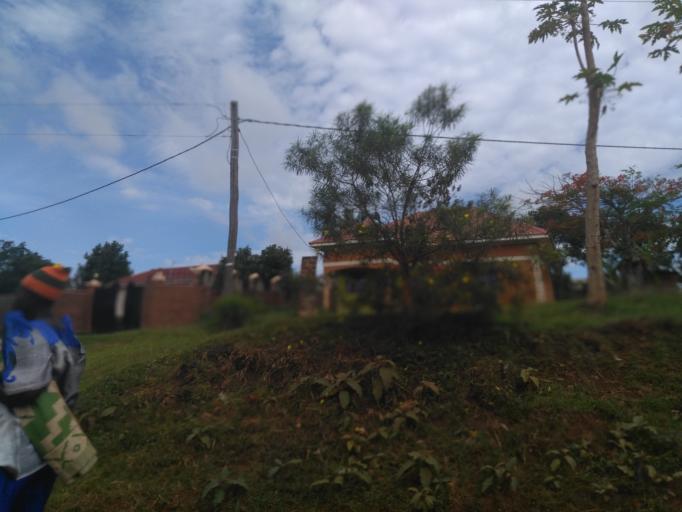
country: UG
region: Central Region
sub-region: Buikwe District
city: Njeru
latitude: 0.4106
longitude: 33.1812
